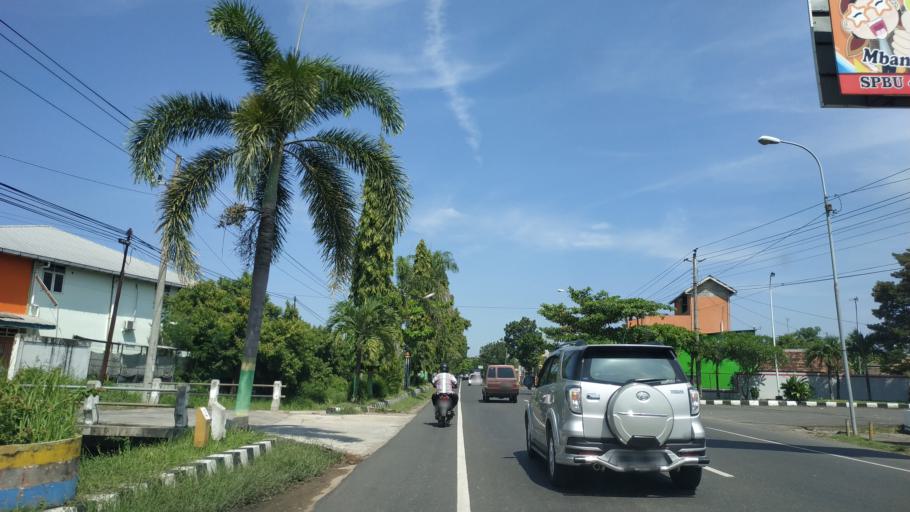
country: ID
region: Central Java
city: Baran
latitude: -6.7508
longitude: 111.0558
